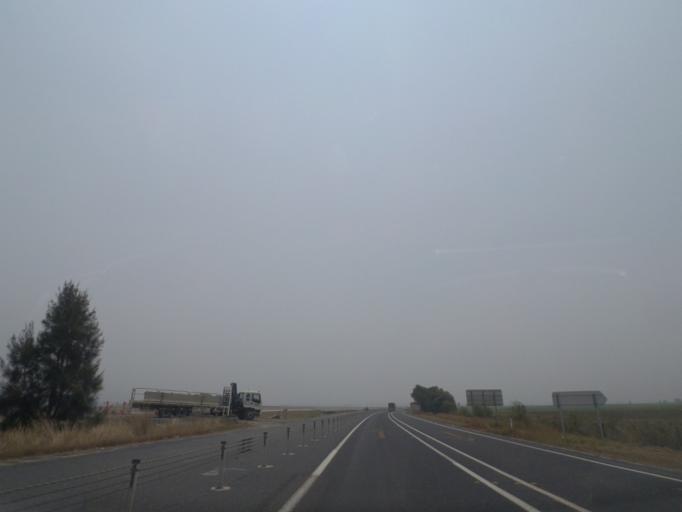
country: AU
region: New South Wales
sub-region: Clarence Valley
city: Maclean
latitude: -29.3895
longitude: 153.2404
